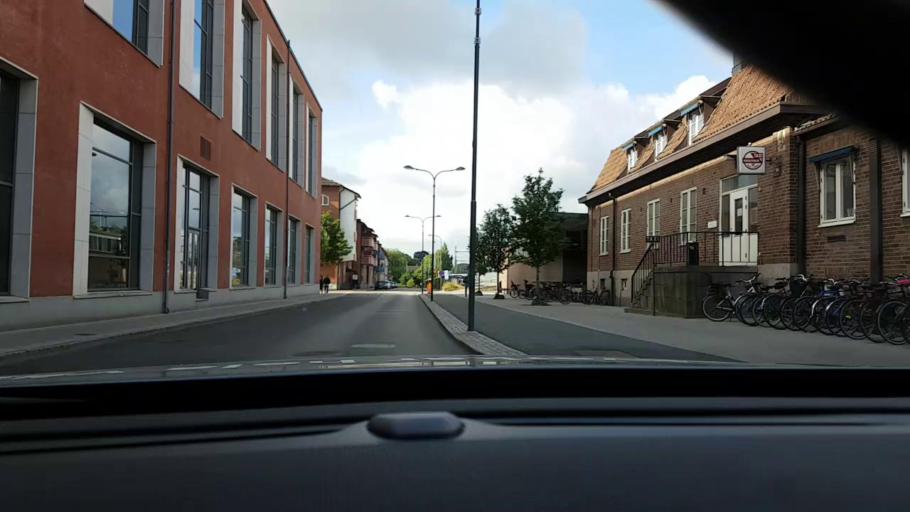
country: SE
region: Skane
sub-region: Hassleholms Kommun
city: Hassleholm
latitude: 56.1573
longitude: 13.7637
